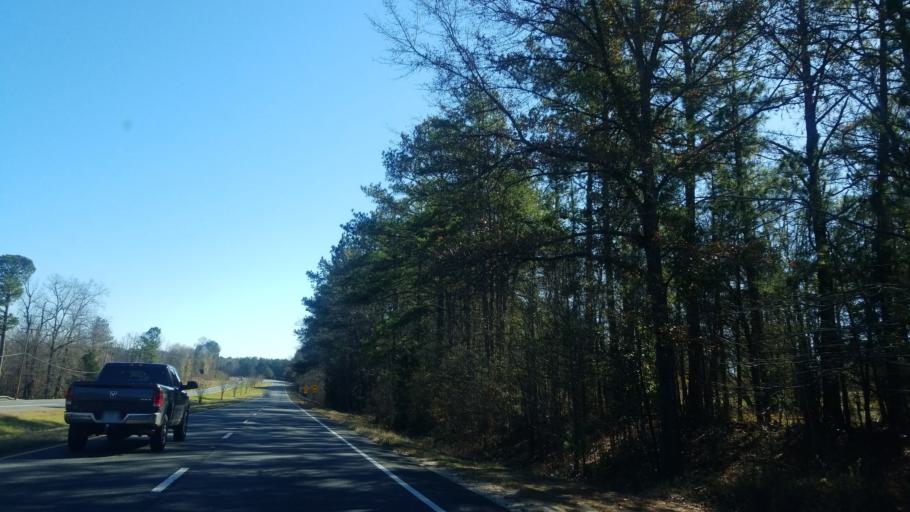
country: US
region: Georgia
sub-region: Talbot County
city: Talbotton
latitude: 32.5490
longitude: -84.7322
